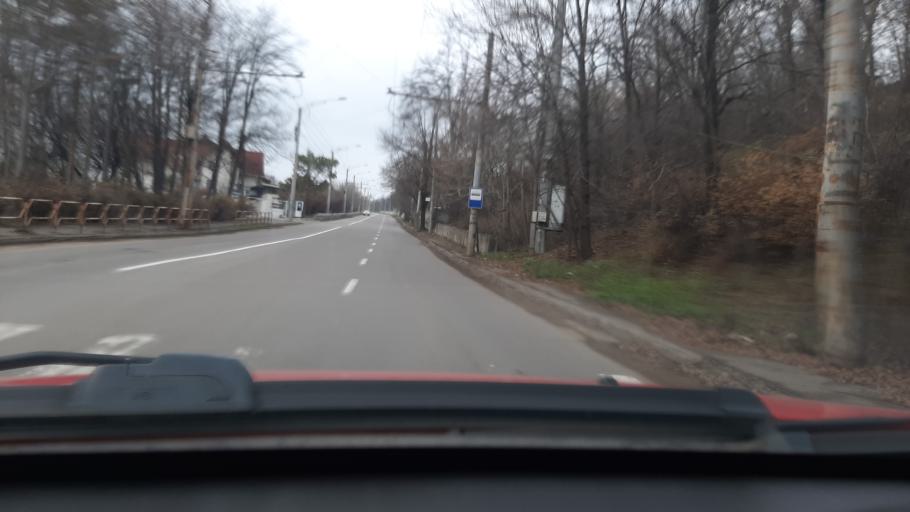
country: MD
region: Chisinau
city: Chisinau
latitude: 47.0503
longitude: 28.8219
